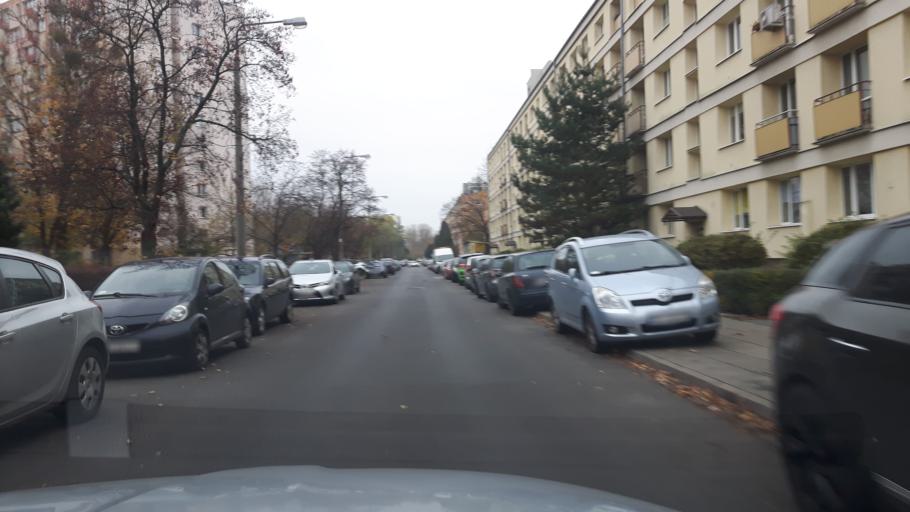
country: PL
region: Masovian Voivodeship
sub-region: Warszawa
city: Praga Polnoc
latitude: 52.2644
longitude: 21.0272
